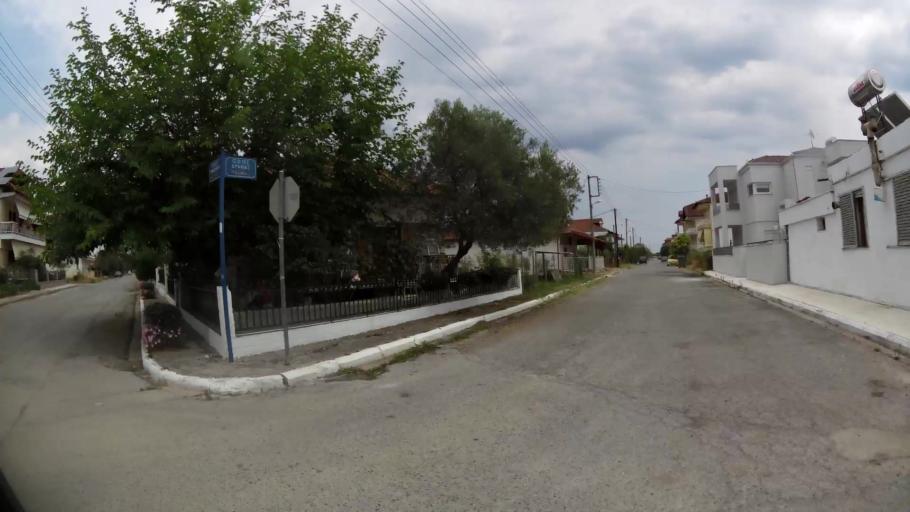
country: GR
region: Central Macedonia
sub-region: Nomos Pierias
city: Kallithea
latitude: 40.2721
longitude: 22.5761
